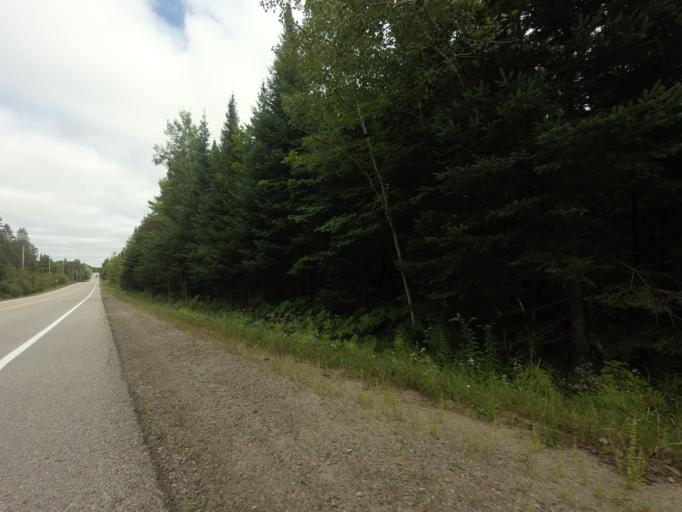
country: CA
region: Ontario
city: Bancroft
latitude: 44.9003
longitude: -78.4376
